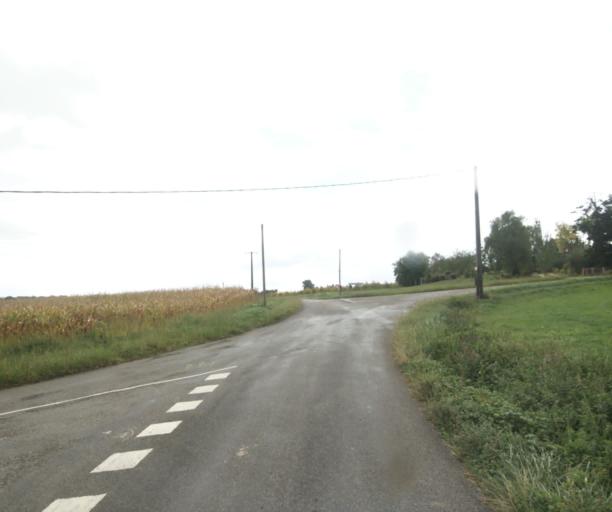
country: FR
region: Midi-Pyrenees
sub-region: Departement du Gers
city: Eauze
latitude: 43.8716
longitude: 0.0692
